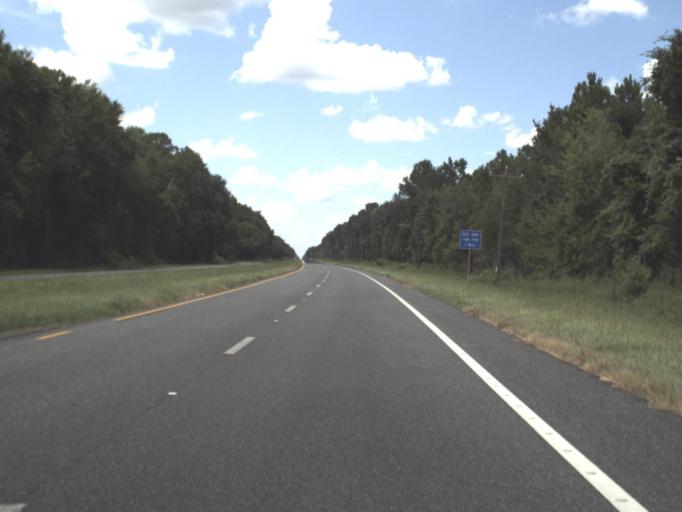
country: US
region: Florida
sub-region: Taylor County
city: Perry
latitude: 30.1883
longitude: -83.6439
